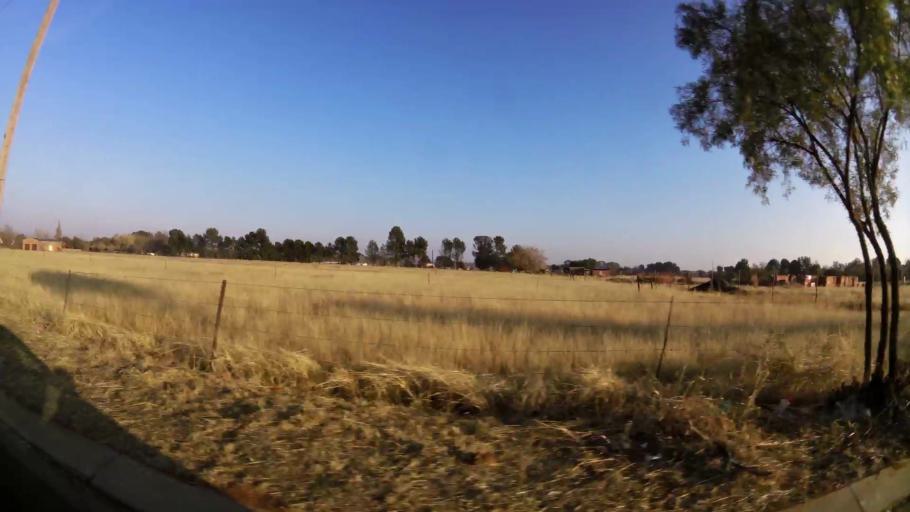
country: ZA
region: Orange Free State
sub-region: Mangaung Metropolitan Municipality
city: Bloemfontein
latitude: -29.0868
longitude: 26.1433
